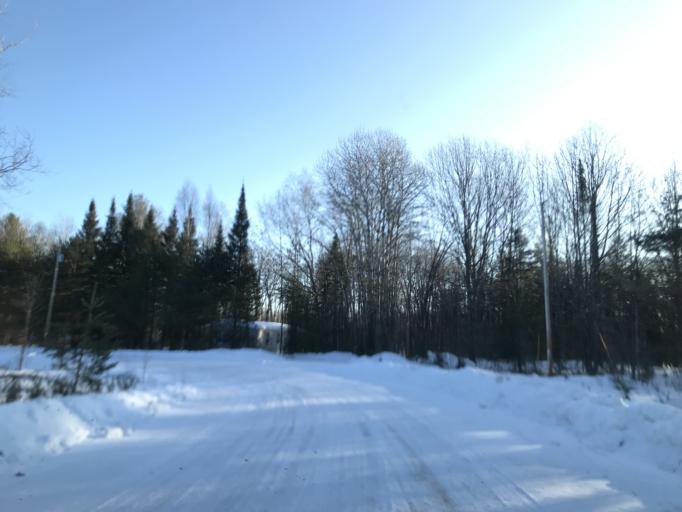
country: US
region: Michigan
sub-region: Menominee County
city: Menominee
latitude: 45.2903
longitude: -87.6962
